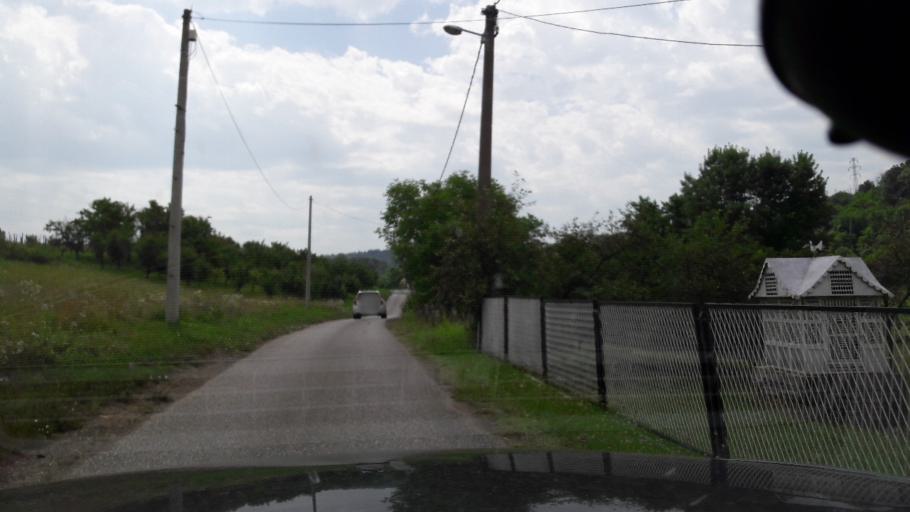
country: RS
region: Central Serbia
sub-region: Belgrade
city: Sopot
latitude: 44.6300
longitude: 20.5950
